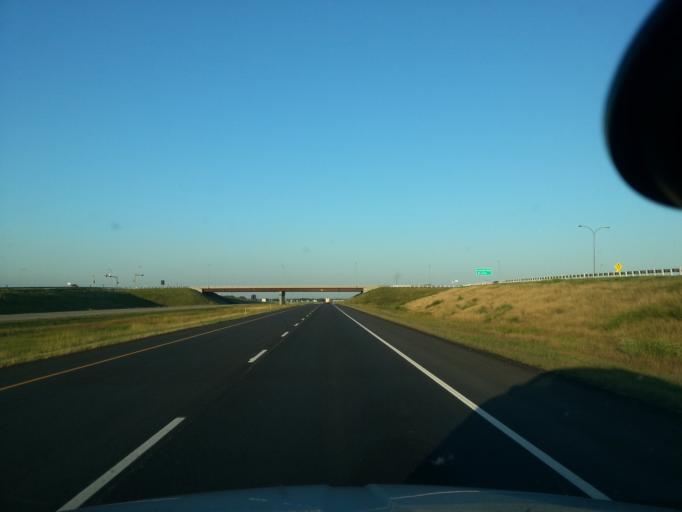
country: CA
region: Alberta
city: Spruce Grove
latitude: 53.5691
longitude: -113.9382
